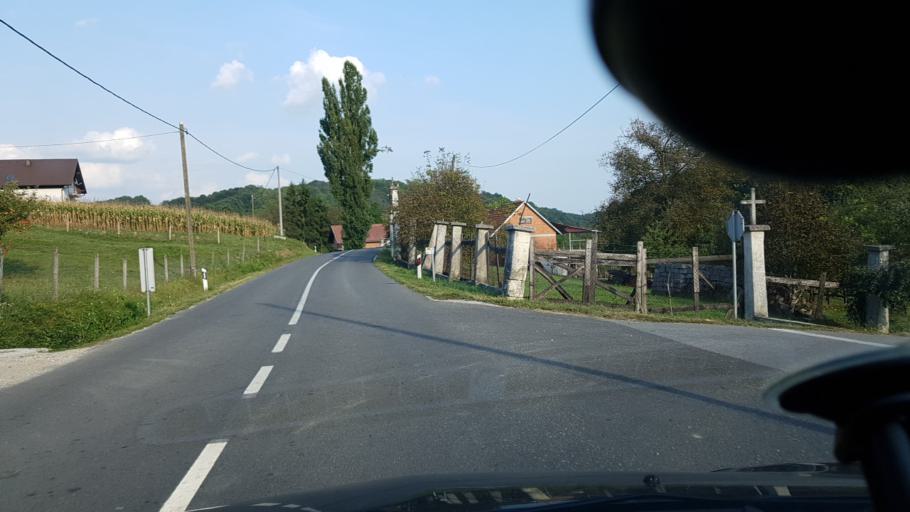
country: HR
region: Krapinsko-Zagorska
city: Pregrada
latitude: 46.1503
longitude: 15.6862
